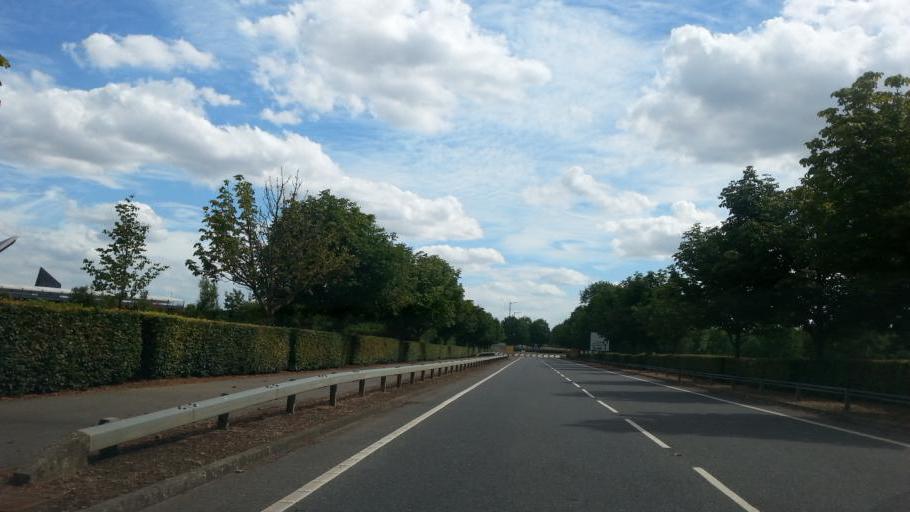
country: GB
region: England
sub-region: Northamptonshire
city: Silverstone
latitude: 52.0703
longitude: -1.0258
